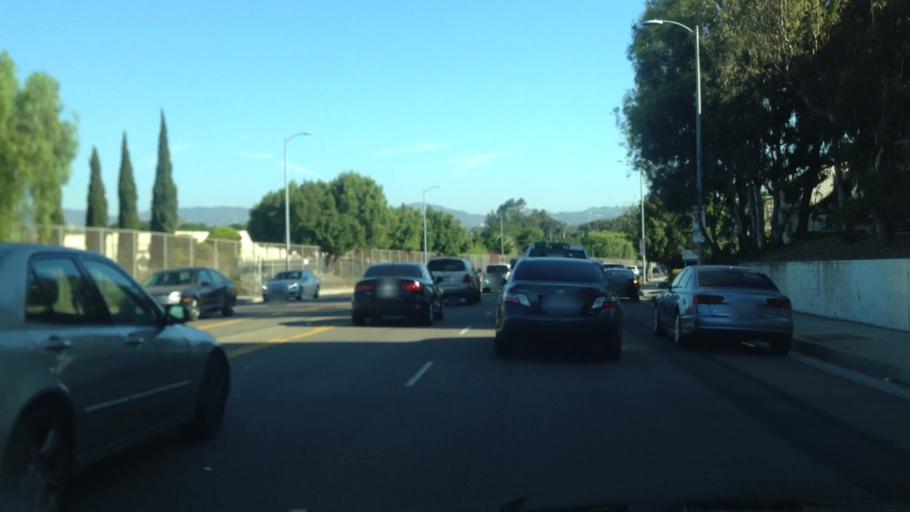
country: US
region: California
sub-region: Los Angeles County
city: Marina del Rey
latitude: 34.0185
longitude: -118.4445
